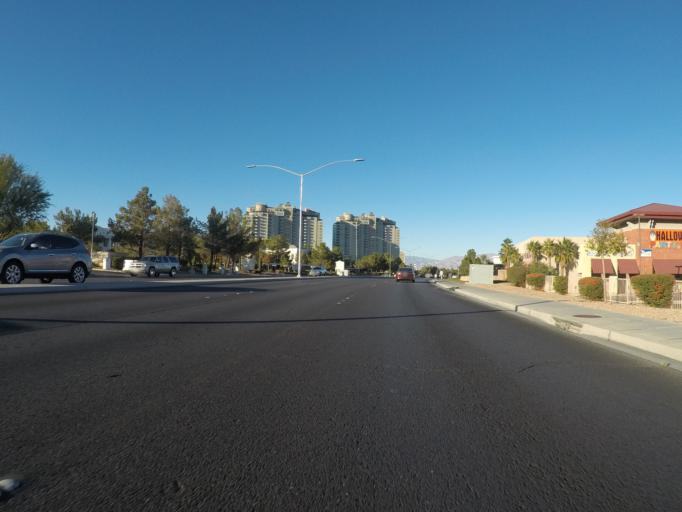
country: US
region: Nevada
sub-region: Clark County
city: Summerlin South
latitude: 36.1622
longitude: -115.2913
